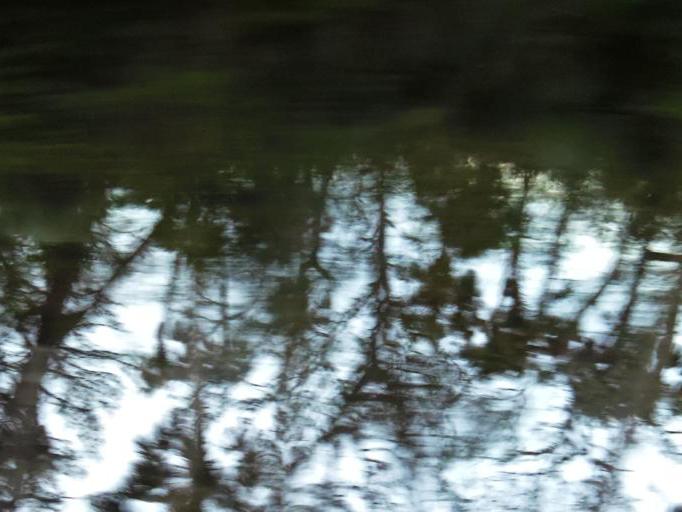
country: US
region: Florida
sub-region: Duval County
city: Atlantic Beach
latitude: 30.3693
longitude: -81.4001
